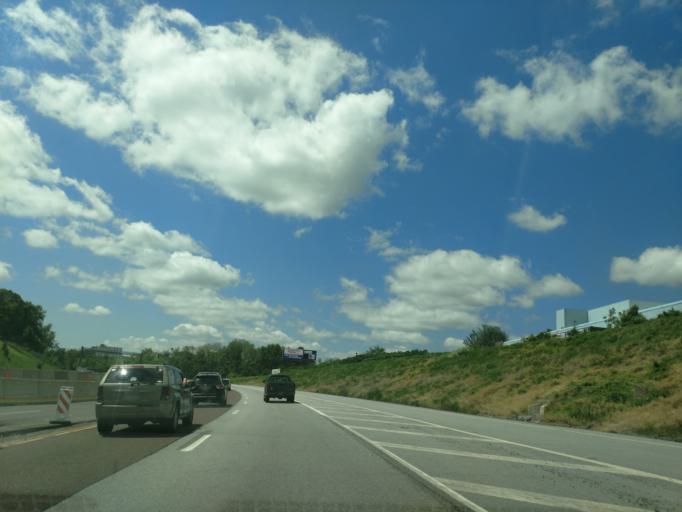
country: US
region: Pennsylvania
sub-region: Montgomery County
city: Audubon
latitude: 40.1155
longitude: -75.4225
